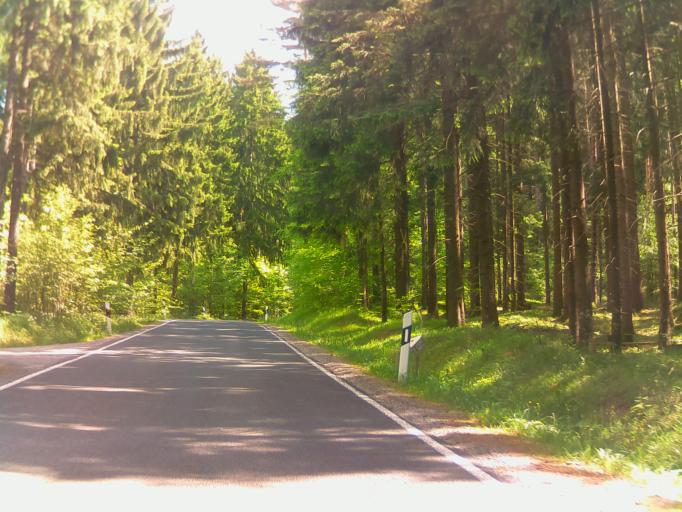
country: DE
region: Thuringia
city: Schmeheim
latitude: 50.5845
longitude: 10.5824
